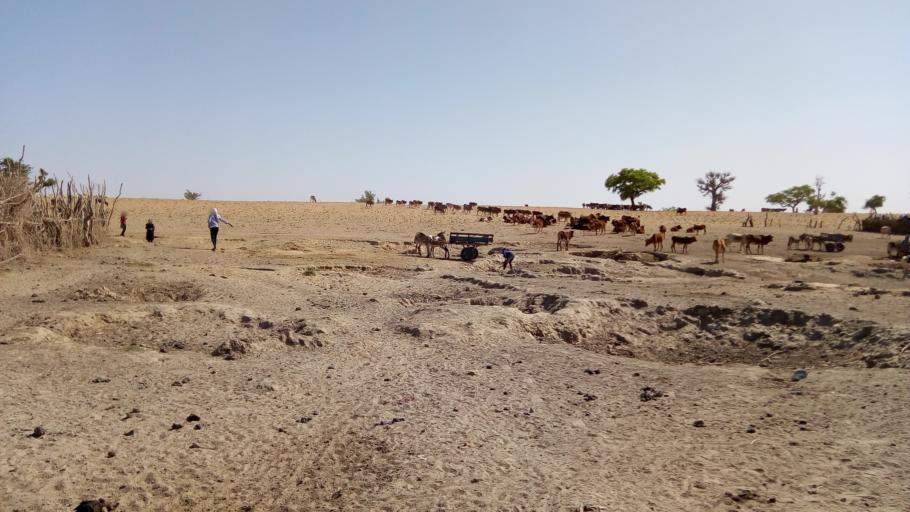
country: ML
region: Kayes
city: Diema
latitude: 14.5142
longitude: -8.8385
